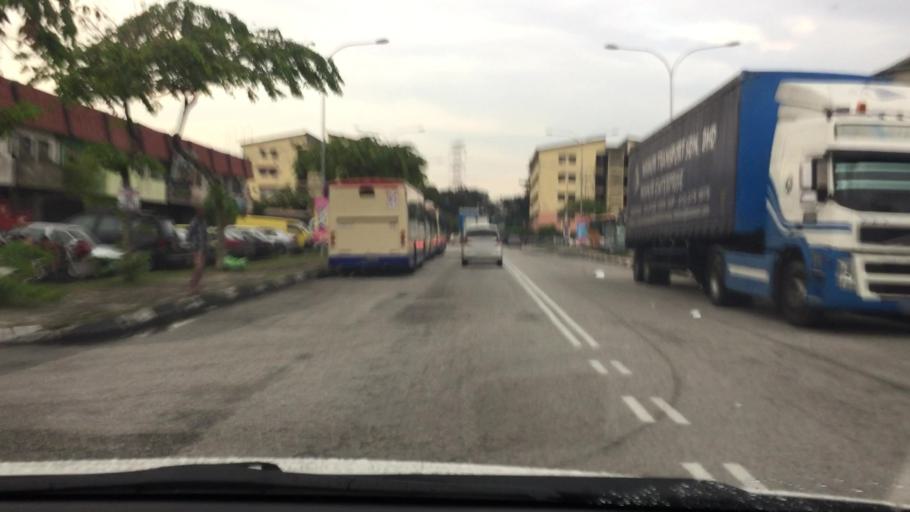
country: MY
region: Selangor
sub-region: Petaling
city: Petaling Jaya
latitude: 3.0753
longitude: 101.6441
